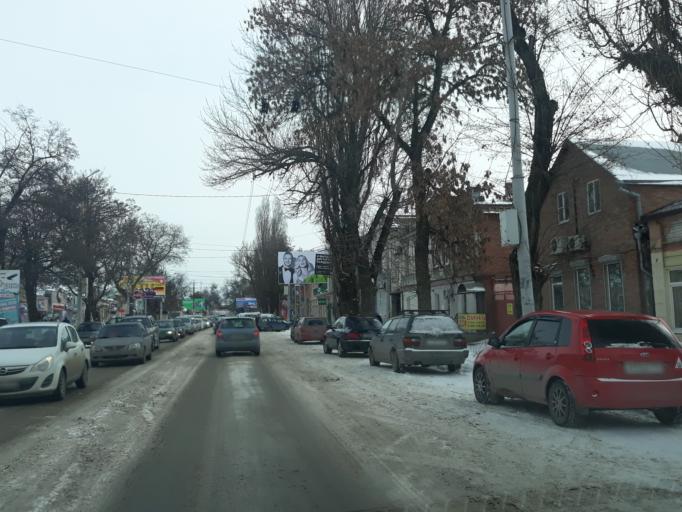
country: RU
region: Rostov
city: Taganrog
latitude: 47.2137
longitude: 38.9126
